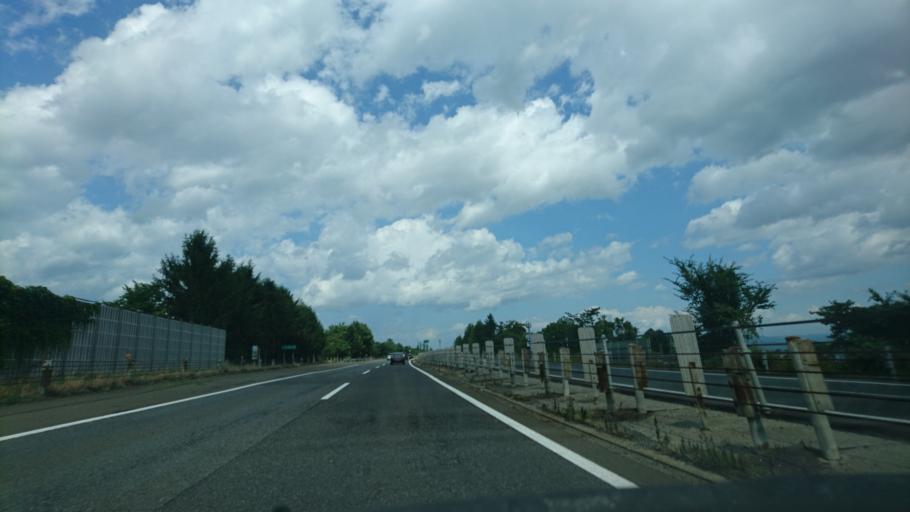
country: JP
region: Iwate
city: Morioka-shi
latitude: 39.5909
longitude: 141.1176
